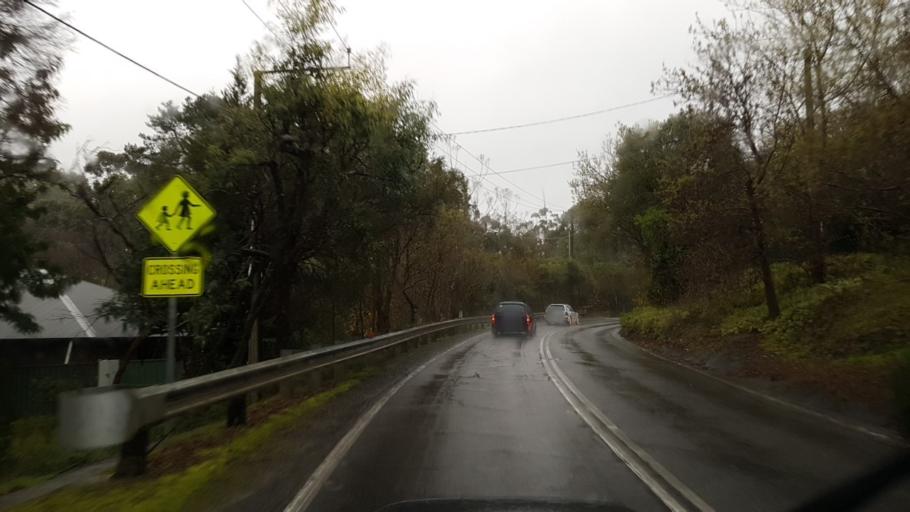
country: AU
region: South Australia
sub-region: Mitcham
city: Blackwood
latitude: -35.0339
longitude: 138.6246
